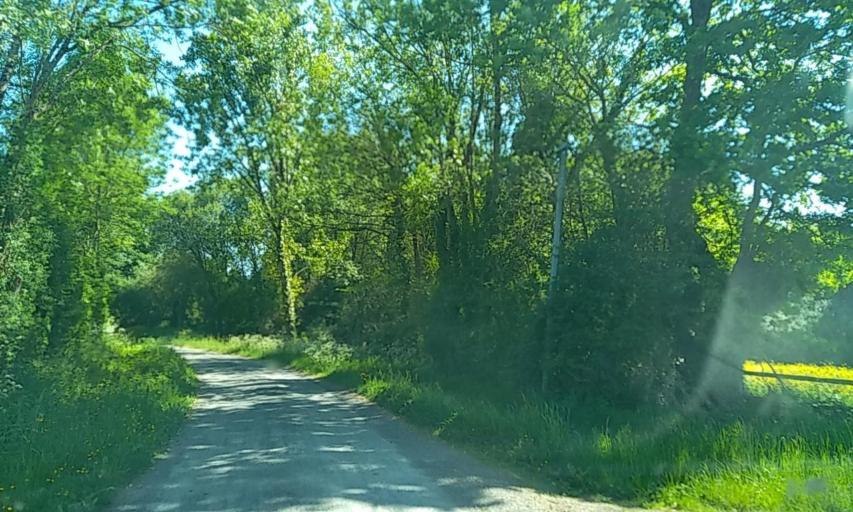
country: FR
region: Poitou-Charentes
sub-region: Departement des Deux-Sevres
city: Boisme
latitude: 46.7664
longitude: -0.4515
